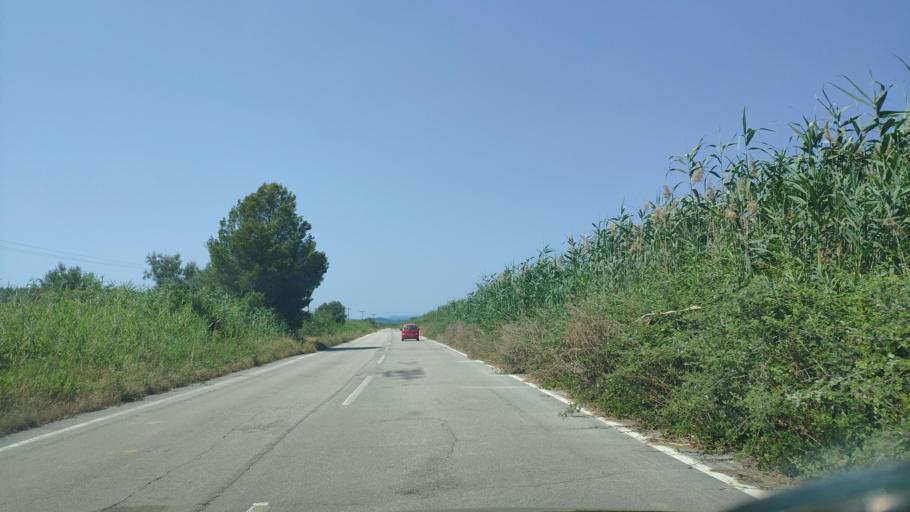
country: GR
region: Epirus
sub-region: Nomos Artas
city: Aneza
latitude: 39.0556
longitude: 20.8647
